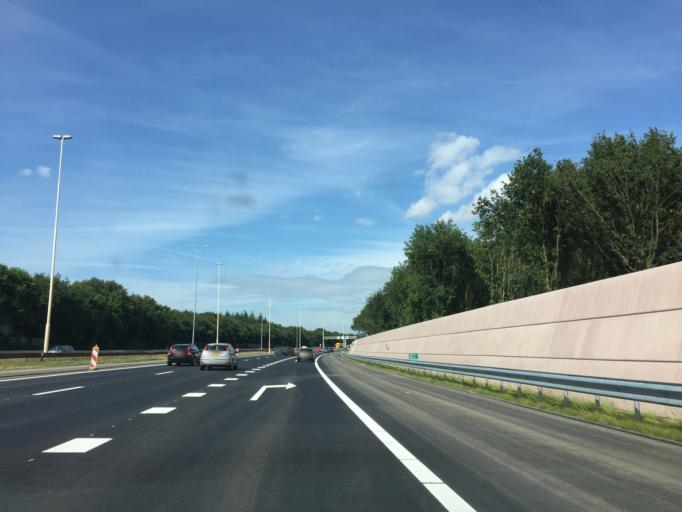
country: NL
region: North Holland
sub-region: Gemeente Laren
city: Laren
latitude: 52.2243
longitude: 5.2240
